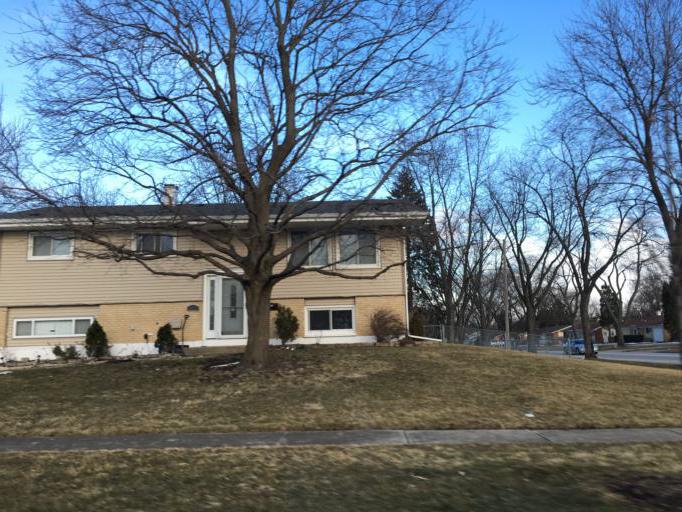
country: US
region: Illinois
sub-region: Cook County
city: Schaumburg
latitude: 42.0415
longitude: -88.0975
